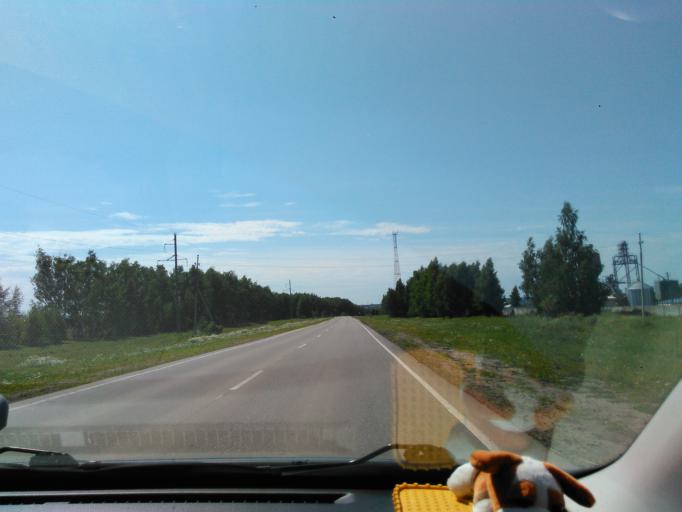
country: RU
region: Penza
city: Belinskiy
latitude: 52.9678
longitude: 43.4623
